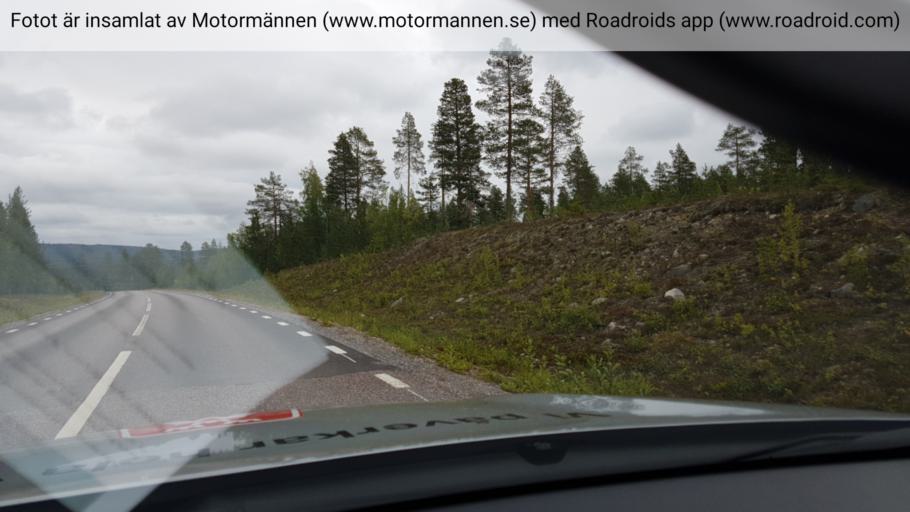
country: SE
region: Norrbotten
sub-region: Gallivare Kommun
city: Gaellivare
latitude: 67.0701
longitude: 21.3201
